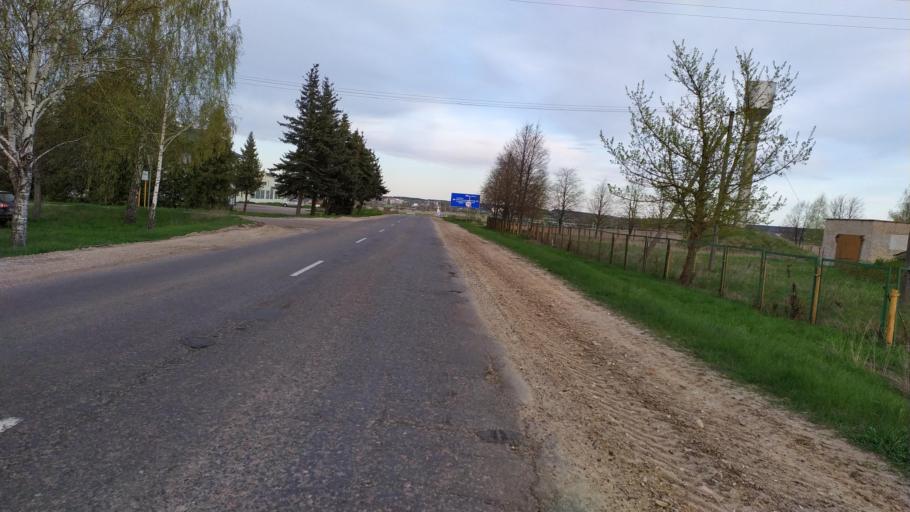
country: BY
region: Brest
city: Kamyanyets
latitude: 52.4002
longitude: 23.7783
